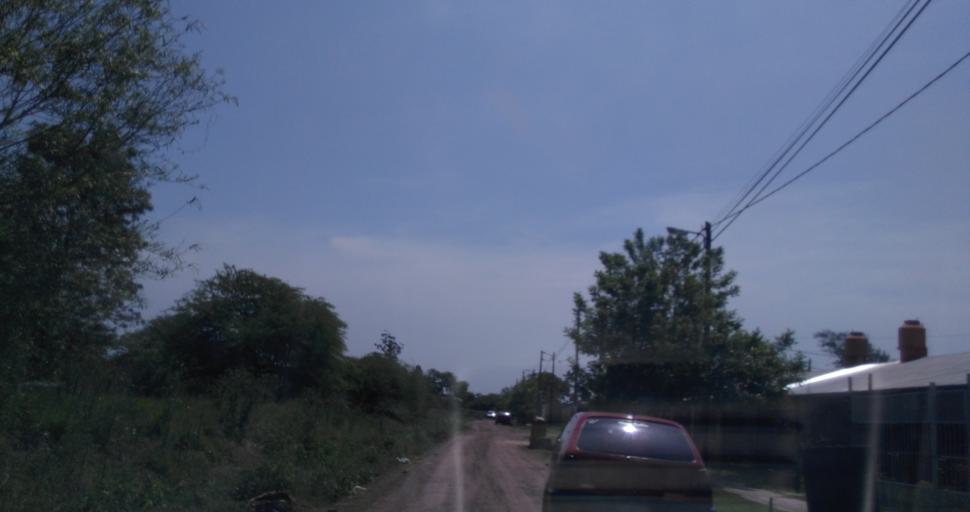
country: AR
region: Chaco
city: Fontana
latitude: -27.3977
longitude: -59.0005
